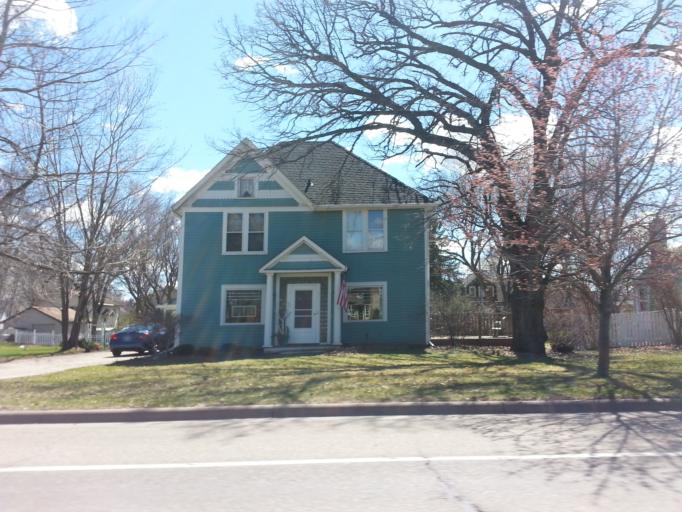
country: US
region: Minnesota
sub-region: Dakota County
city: Hastings
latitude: 44.7443
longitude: -92.8645
